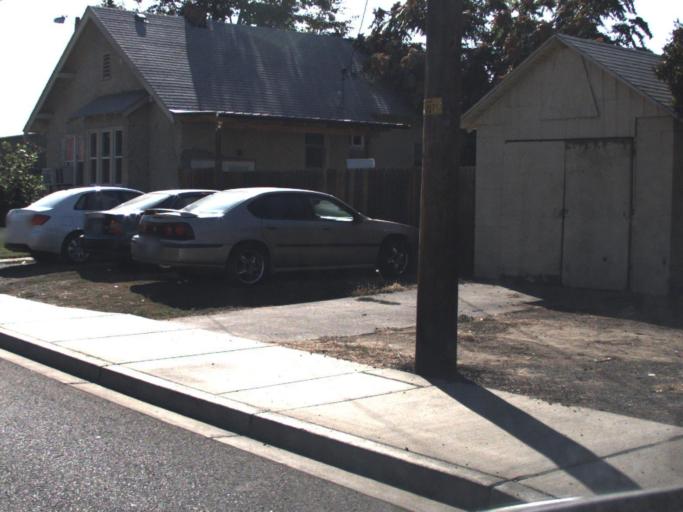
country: US
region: Washington
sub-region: Walla Walla County
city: Walla Walla
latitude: 46.0691
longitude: -118.3565
